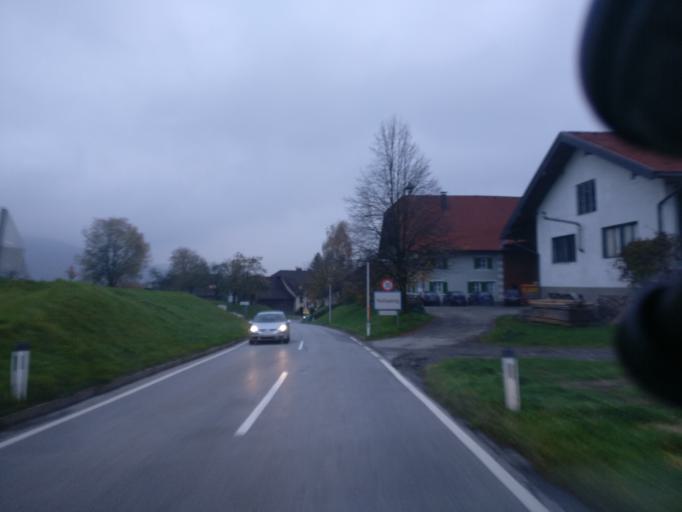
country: AT
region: Salzburg
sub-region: Politischer Bezirk Salzburg-Umgebung
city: Hallwang
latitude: 47.8531
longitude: 13.0818
